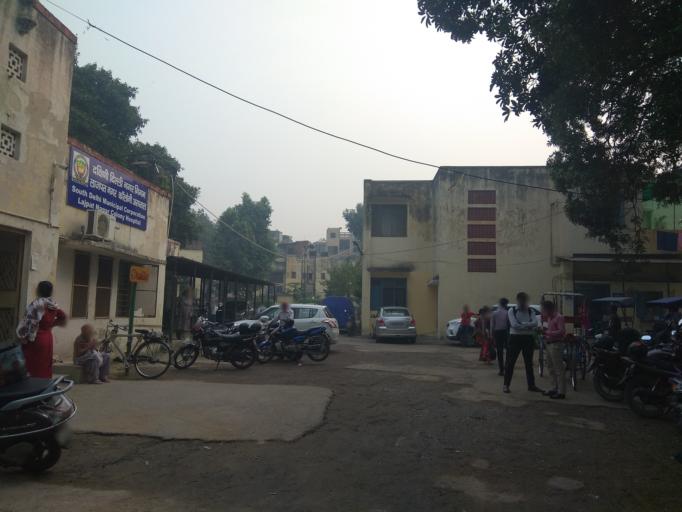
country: IN
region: NCT
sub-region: New Delhi
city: New Delhi
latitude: 28.5690
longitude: 77.2447
